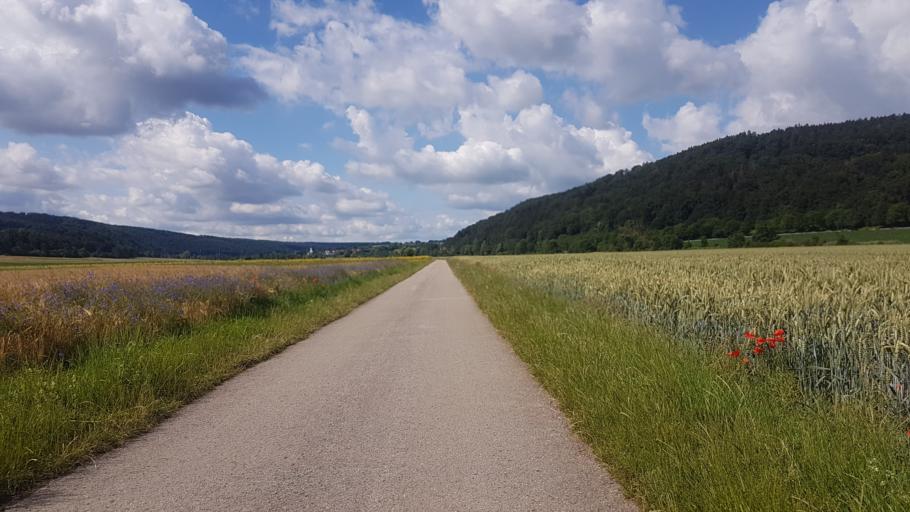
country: DE
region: Bavaria
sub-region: Upper Bavaria
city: Walting
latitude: 48.9315
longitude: 11.3100
